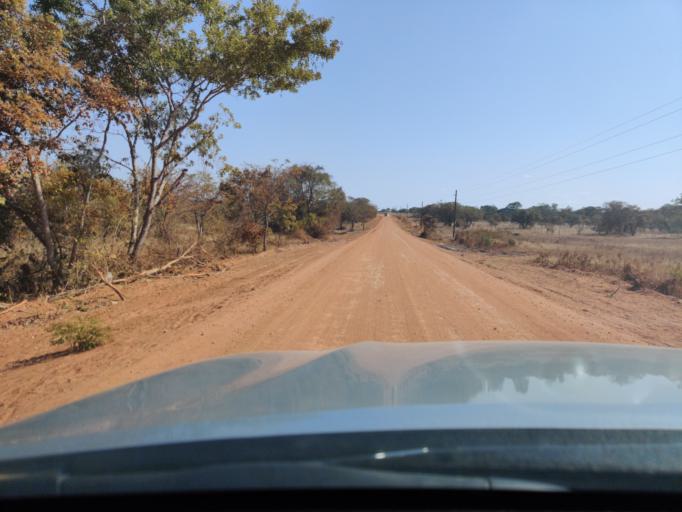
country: ZM
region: Central
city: Mkushi
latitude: -13.9899
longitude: 29.5343
